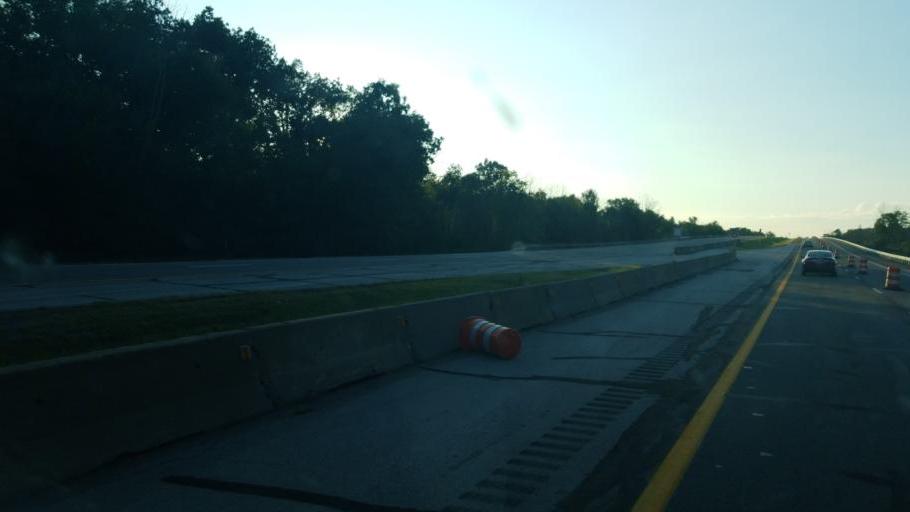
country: US
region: Ohio
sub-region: Mahoning County
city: Austintown
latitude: 41.0633
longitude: -80.7839
